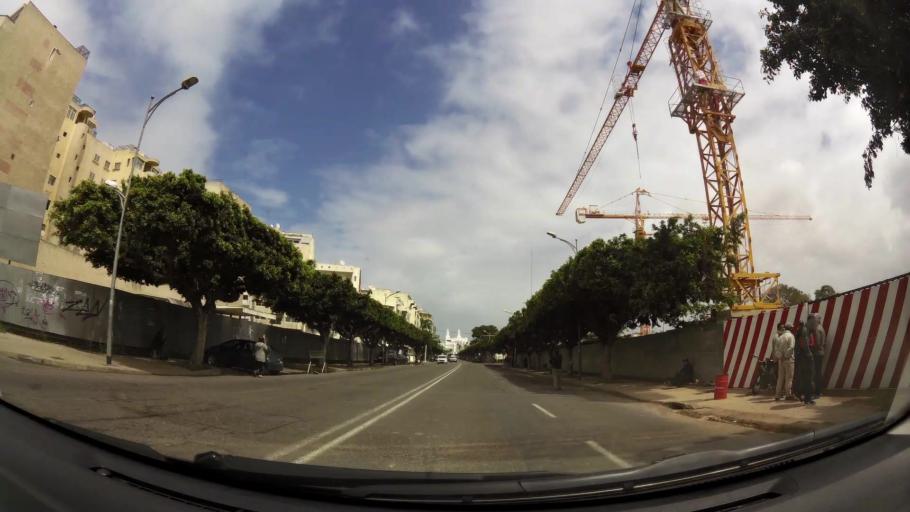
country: MA
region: Grand Casablanca
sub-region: Casablanca
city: Casablanca
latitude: 33.5864
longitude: -7.6289
